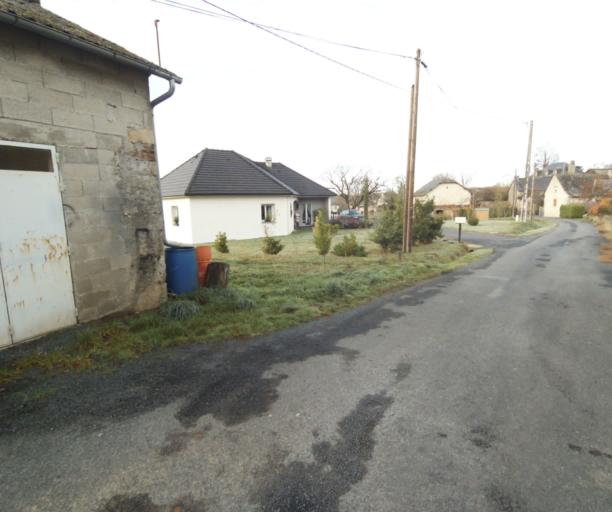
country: FR
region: Limousin
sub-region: Departement de la Correze
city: Cornil
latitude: 45.2129
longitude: 1.7134
